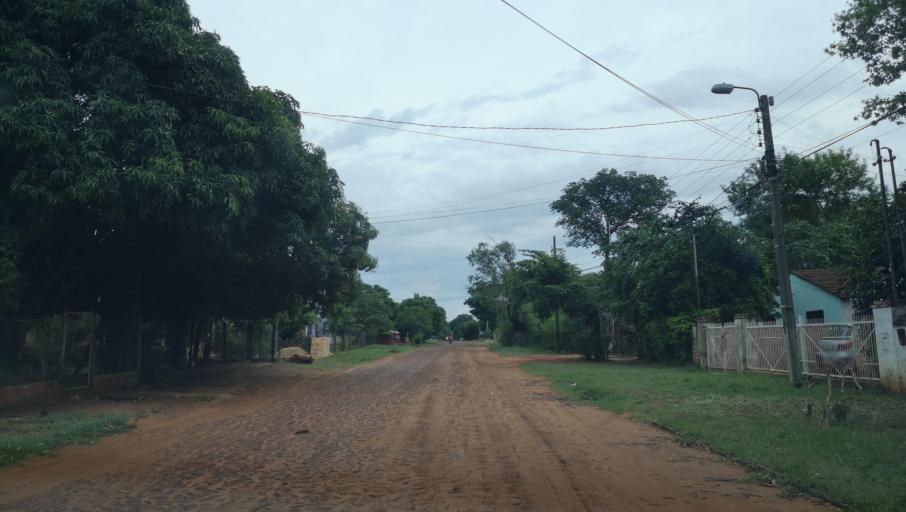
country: PY
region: Misiones
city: Santa Maria
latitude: -26.8909
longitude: -57.0411
